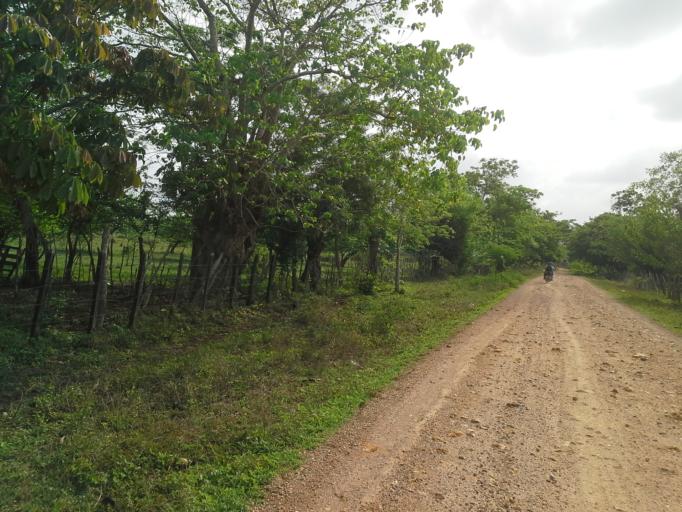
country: CO
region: Cordoba
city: Chima
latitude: 9.1046
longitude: -75.6176
